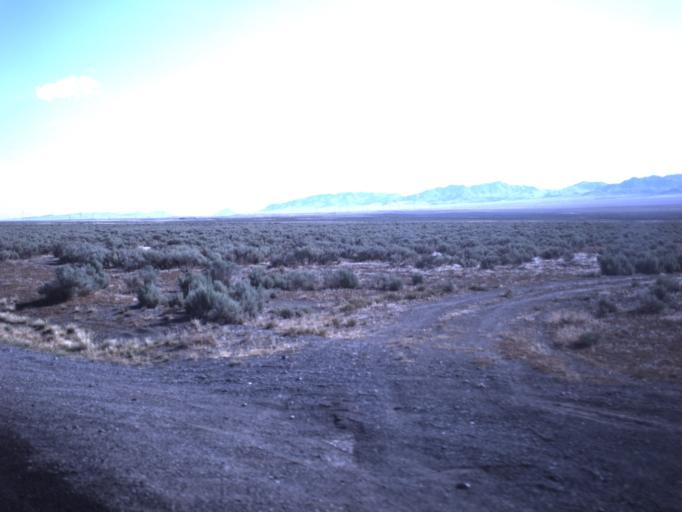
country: US
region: Utah
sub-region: Beaver County
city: Milford
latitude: 38.4263
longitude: -113.0098
